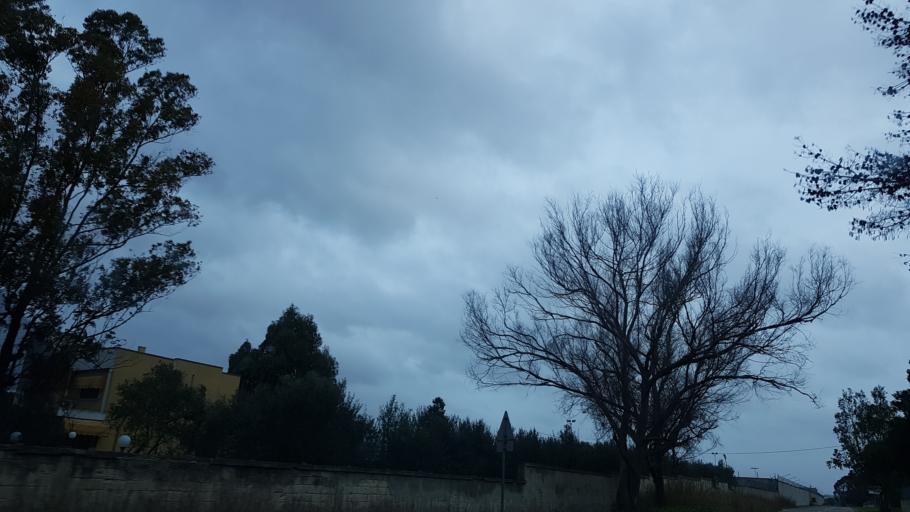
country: IT
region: Apulia
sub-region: Provincia di Brindisi
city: Brindisi
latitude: 40.6345
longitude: 17.9136
